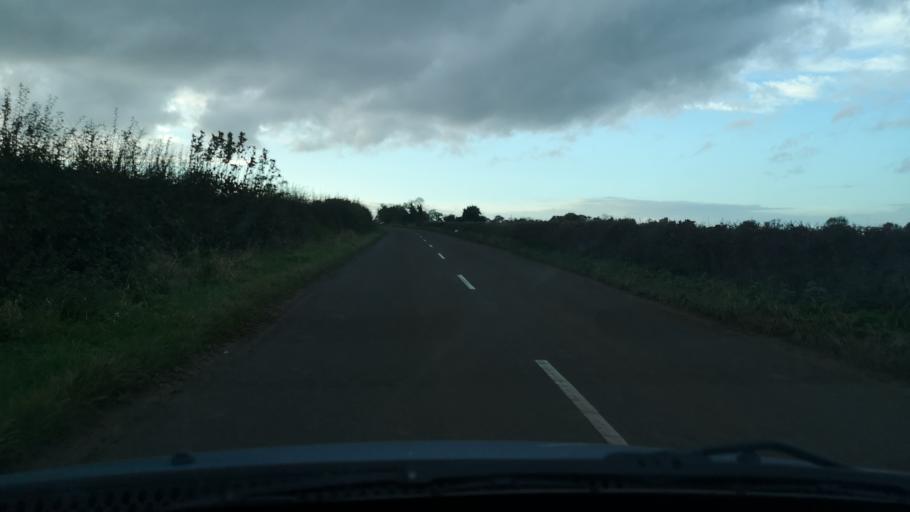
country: GB
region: England
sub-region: Doncaster
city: Norton
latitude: 53.6387
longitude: -1.2115
